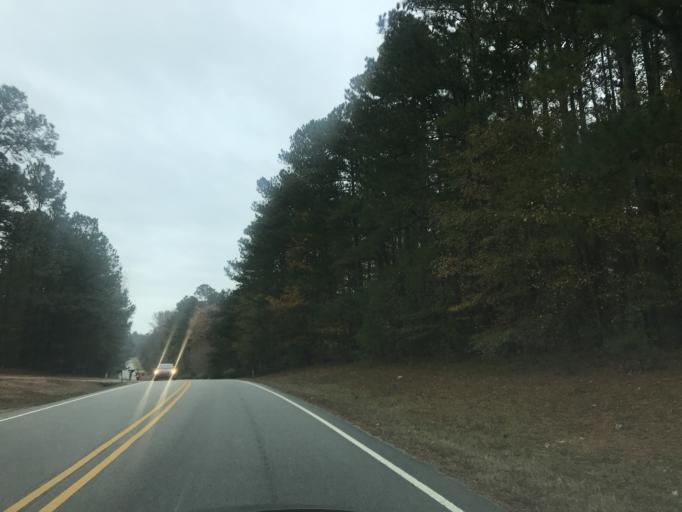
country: US
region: North Carolina
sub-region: Wake County
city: Wake Forest
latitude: 35.9982
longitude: -78.4972
